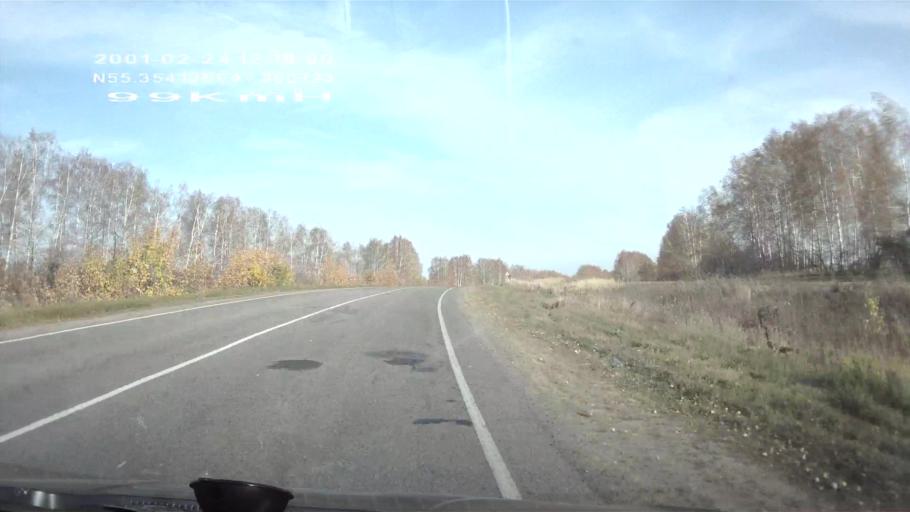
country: RU
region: Chuvashia
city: Ibresi
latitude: 55.3543
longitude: 47.2008
